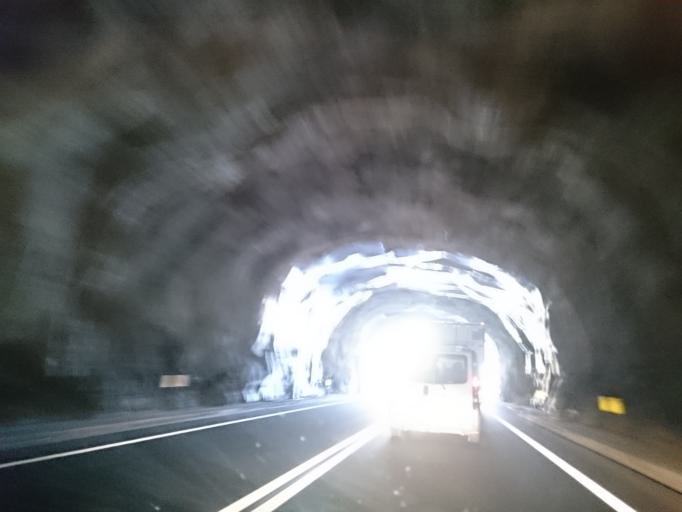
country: ES
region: Catalonia
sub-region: Provincia de Lleida
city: Vielha
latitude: 42.5775
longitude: 0.7563
